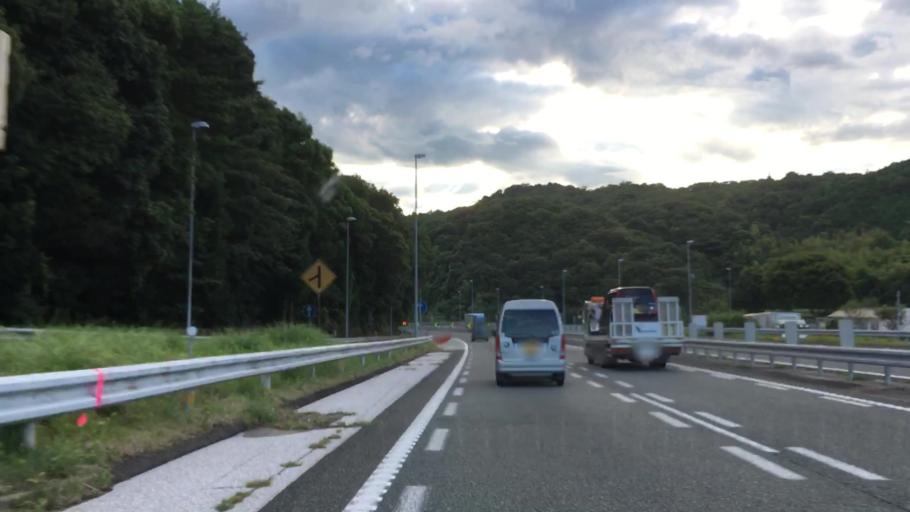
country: JP
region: Yamaguchi
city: Onoda
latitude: 34.1193
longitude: 131.2058
